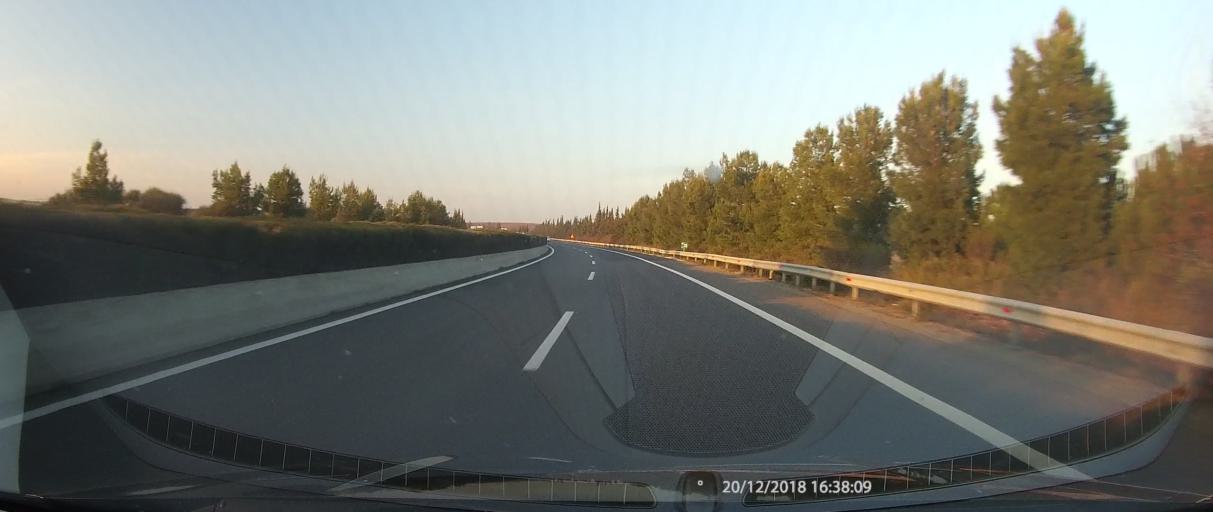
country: GR
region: Thessaly
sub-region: Nomos Magnisias
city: Velestino
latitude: 39.3398
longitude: 22.7837
